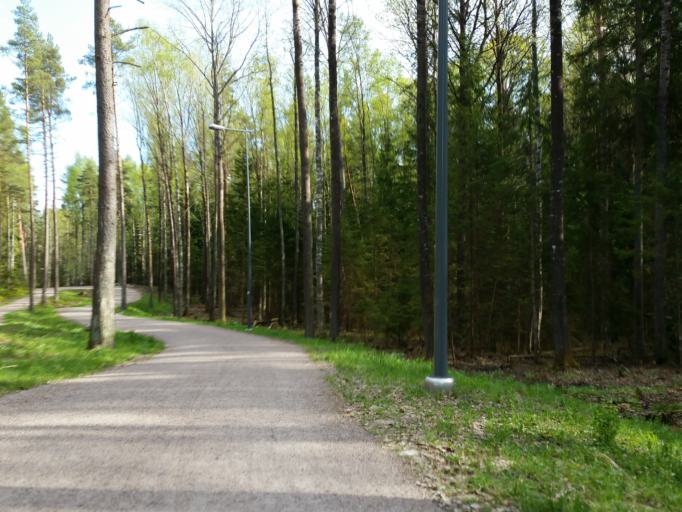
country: FI
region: Uusimaa
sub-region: Helsinki
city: Kauniainen
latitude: 60.1808
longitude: 24.7184
